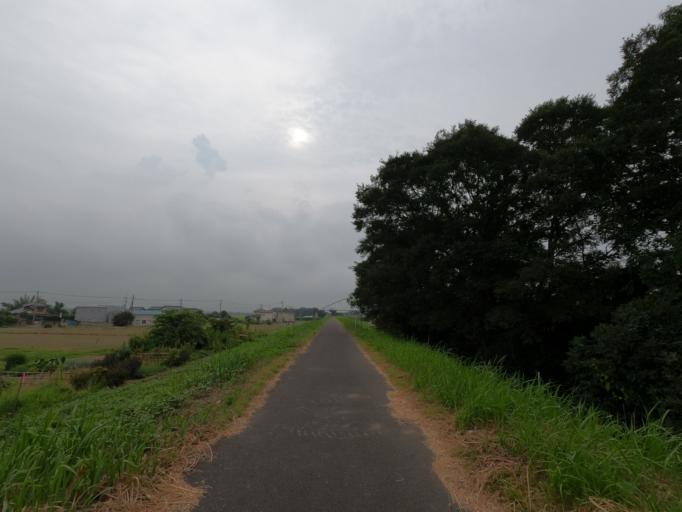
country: JP
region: Ibaraki
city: Moriya
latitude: 35.9574
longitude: 140.0140
